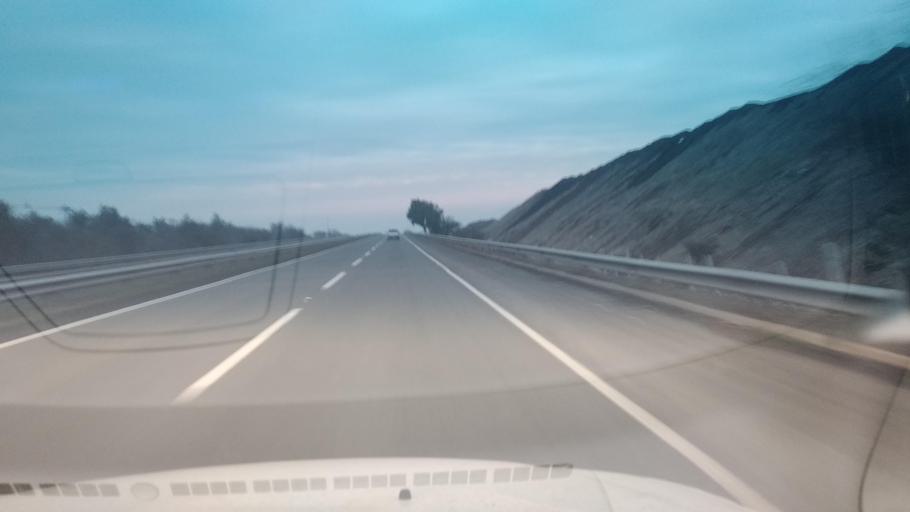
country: CL
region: Santiago Metropolitan
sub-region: Provincia de Chacabuco
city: Chicureo Abajo
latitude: -33.2045
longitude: -70.6652
